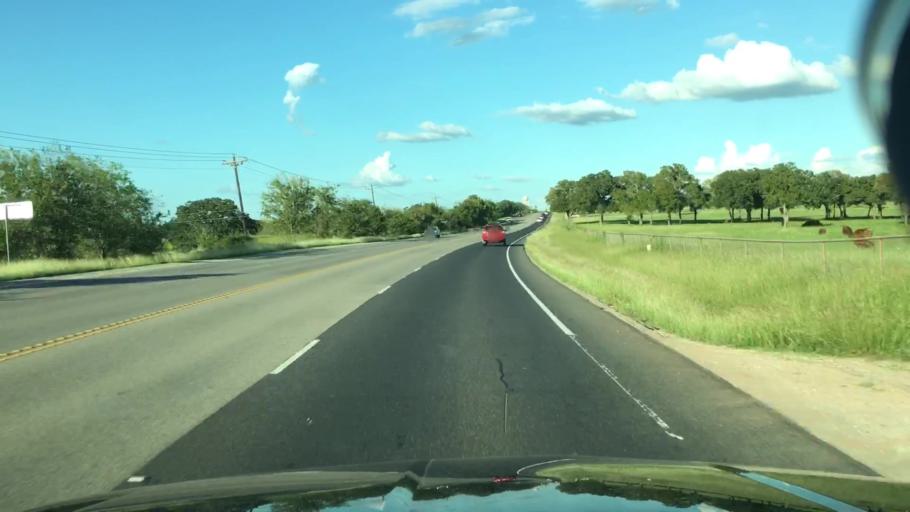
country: US
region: Texas
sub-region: Bastrop County
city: Camp Swift
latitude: 30.2016
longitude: -97.1572
